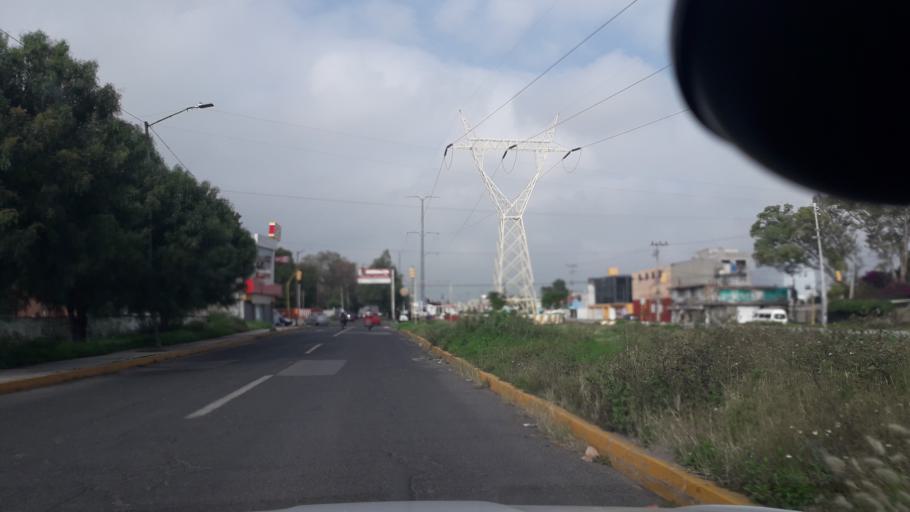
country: MX
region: Mexico
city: Coacalco
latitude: 19.6444
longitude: -99.0932
